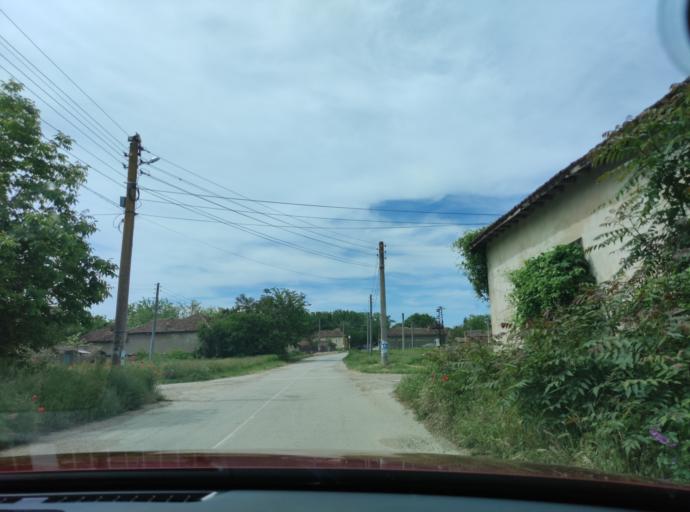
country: BG
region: Pleven
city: Iskur
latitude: 43.5351
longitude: 24.2824
